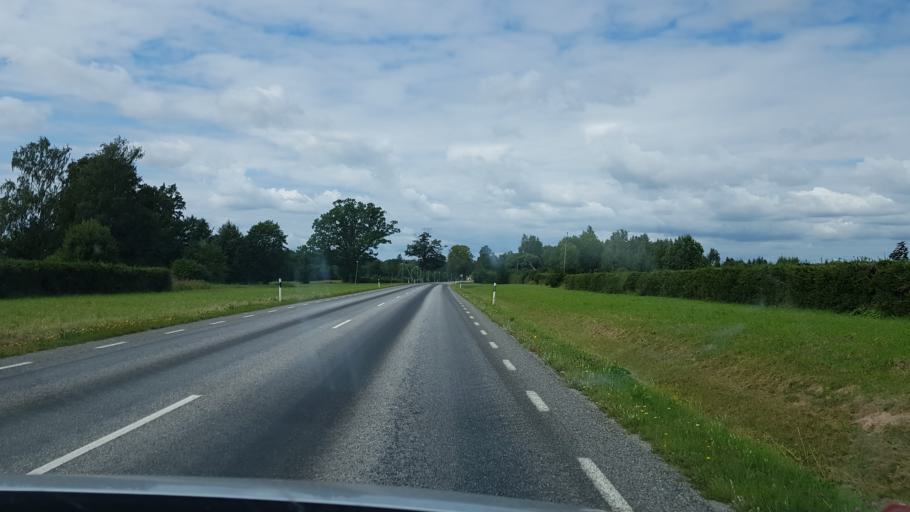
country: EE
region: Tartu
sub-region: Elva linn
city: Elva
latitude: 58.1210
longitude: 26.3331
